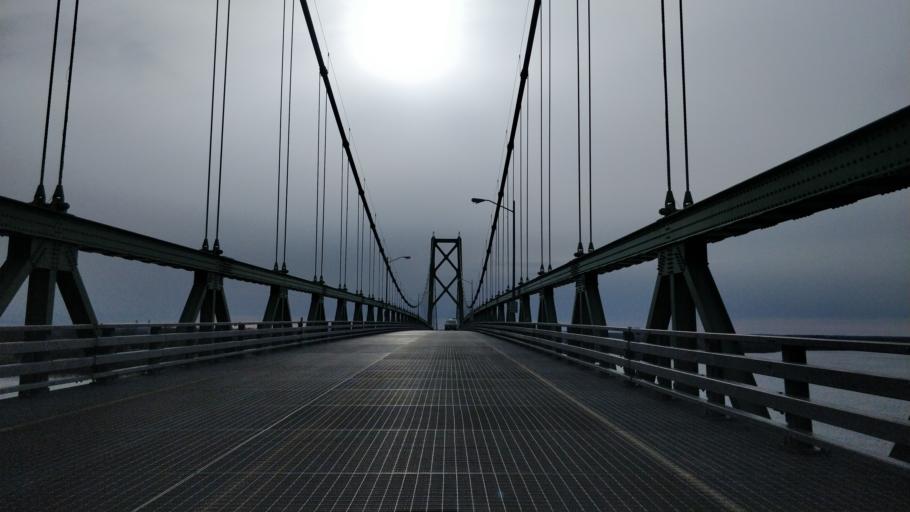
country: US
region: New York
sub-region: St. Lawrence County
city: Ogdensburg
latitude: 44.7362
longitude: -75.4600
